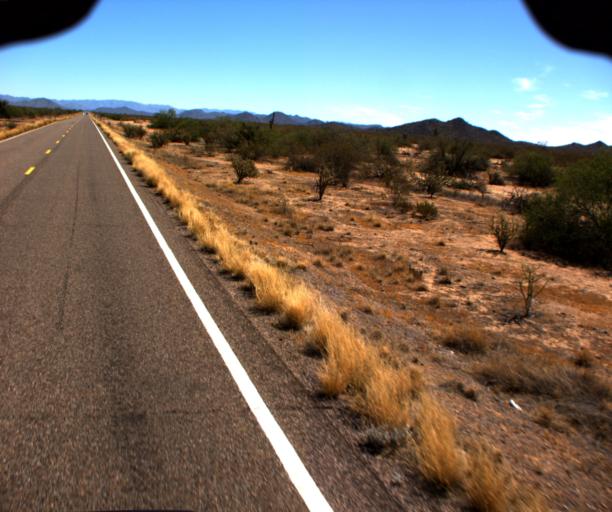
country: US
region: Arizona
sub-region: Yavapai County
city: Congress
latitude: 34.0103
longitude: -113.1088
